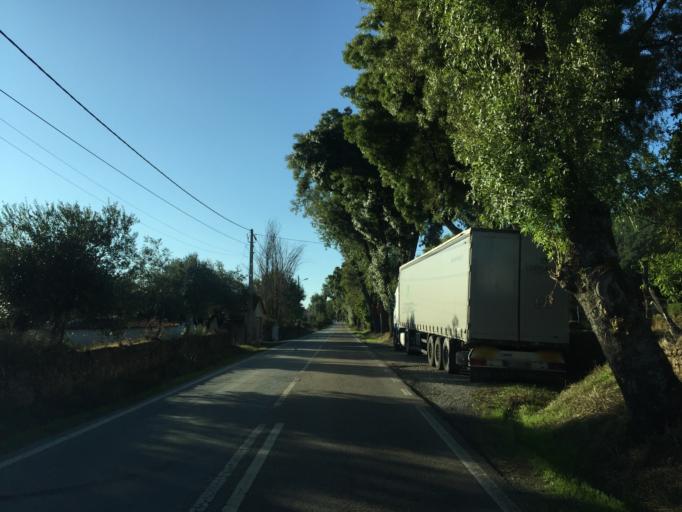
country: PT
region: Portalegre
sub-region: Marvao
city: Marvao
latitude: 39.3909
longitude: -7.4124
